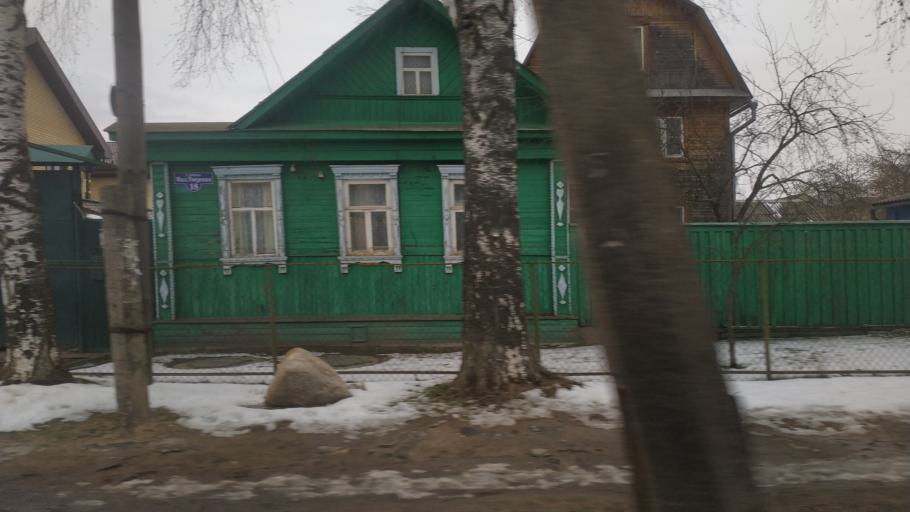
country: RU
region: Tverskaya
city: Tver
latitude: 56.8873
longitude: 35.8973
